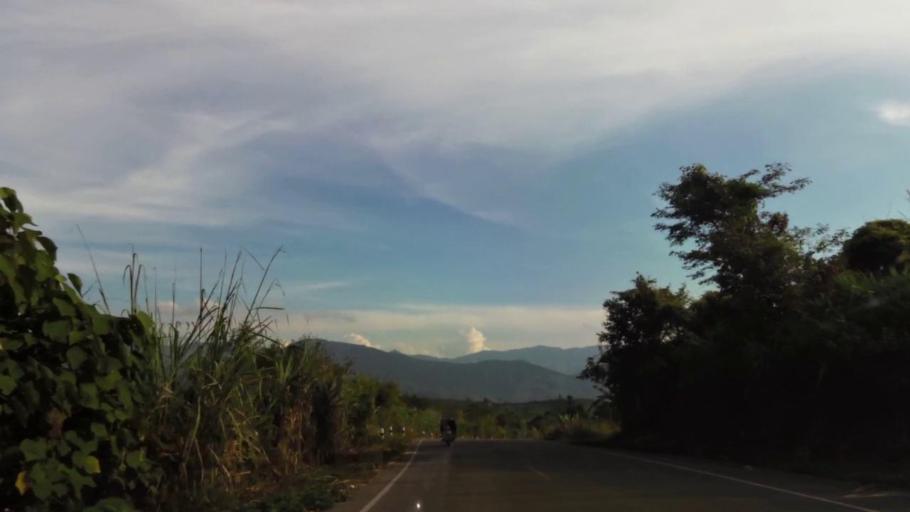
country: TH
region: Chiang Rai
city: Khun Tan
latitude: 19.8620
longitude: 100.3670
